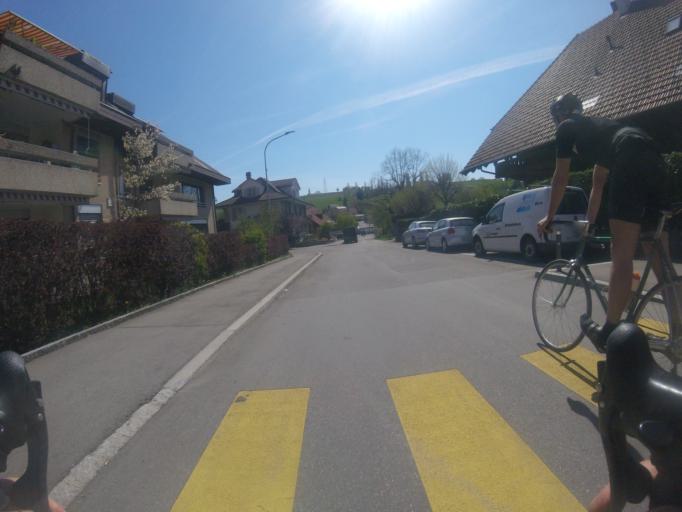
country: CH
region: Bern
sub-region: Bern-Mittelland District
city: Frauenkappelen
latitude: 46.9151
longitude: 7.3601
